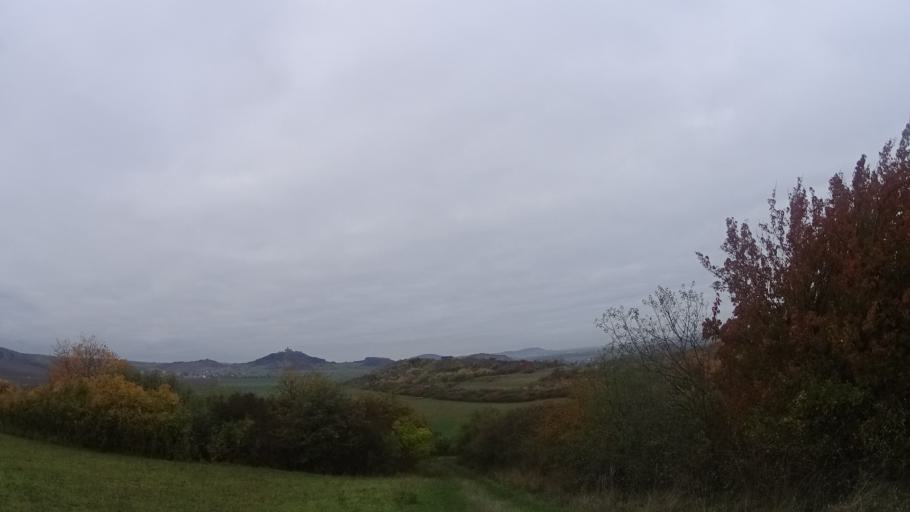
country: DE
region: Thuringia
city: Arnstadt
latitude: 50.8504
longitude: 10.9207
